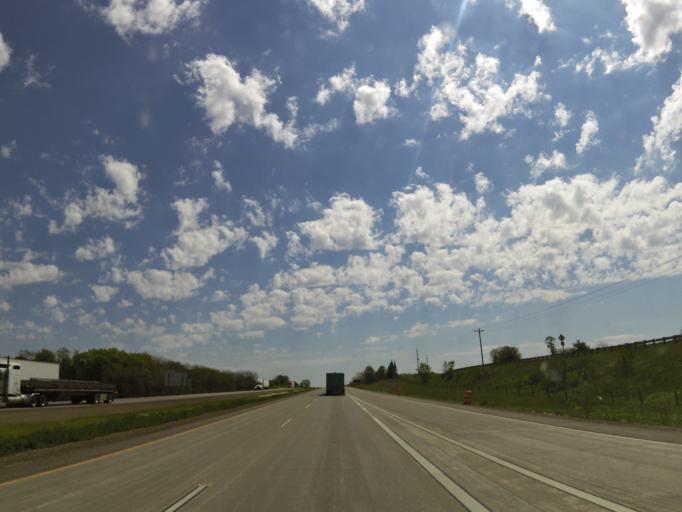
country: US
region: Wisconsin
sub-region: Eau Claire County
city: Altoona
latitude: 44.7656
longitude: -91.4540
